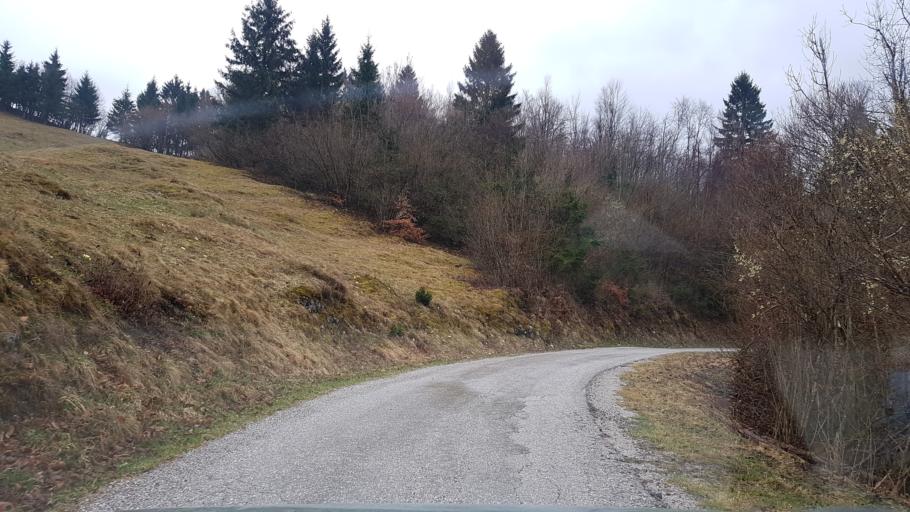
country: SI
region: Cerkno
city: Cerkno
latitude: 46.1393
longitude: 13.8805
